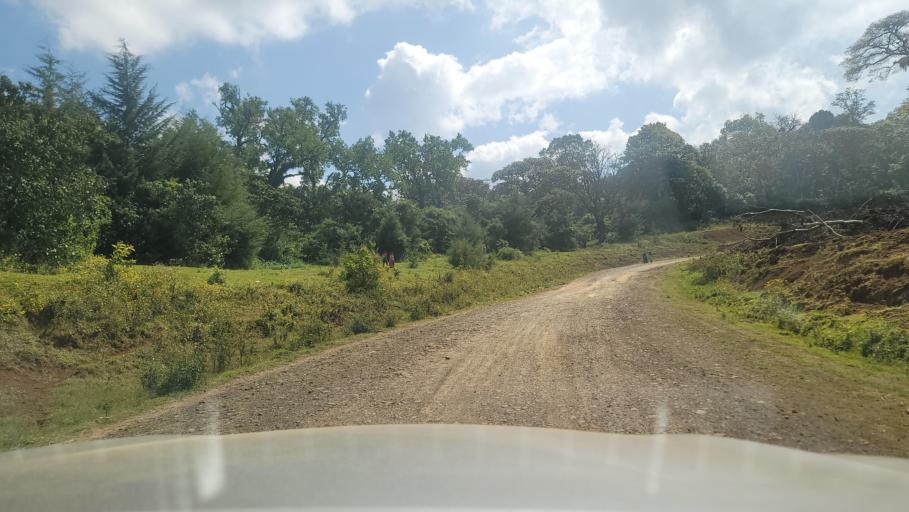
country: ET
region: Oromiya
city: Agaro
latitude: 7.7212
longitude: 36.2597
